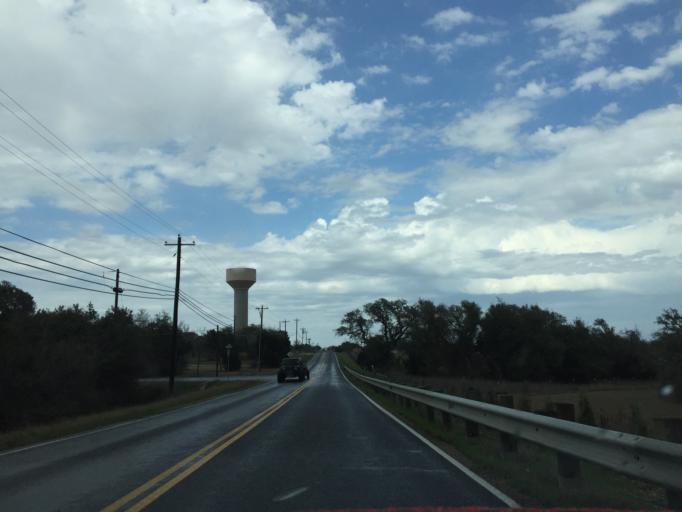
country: US
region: Texas
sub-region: Burnet County
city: Bertram
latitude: 30.6957
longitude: -97.9333
